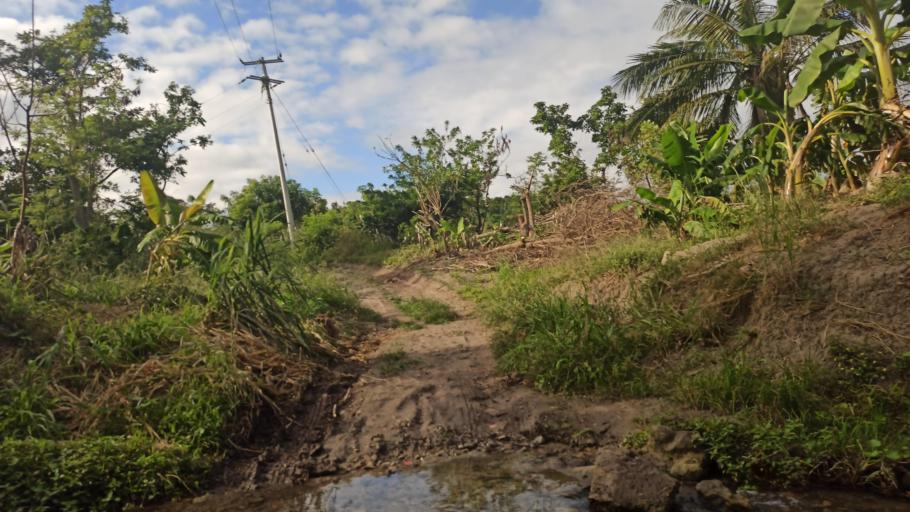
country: MX
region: Veracruz
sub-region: Papantla
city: Residencial Tajin
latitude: 20.6451
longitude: -97.3609
